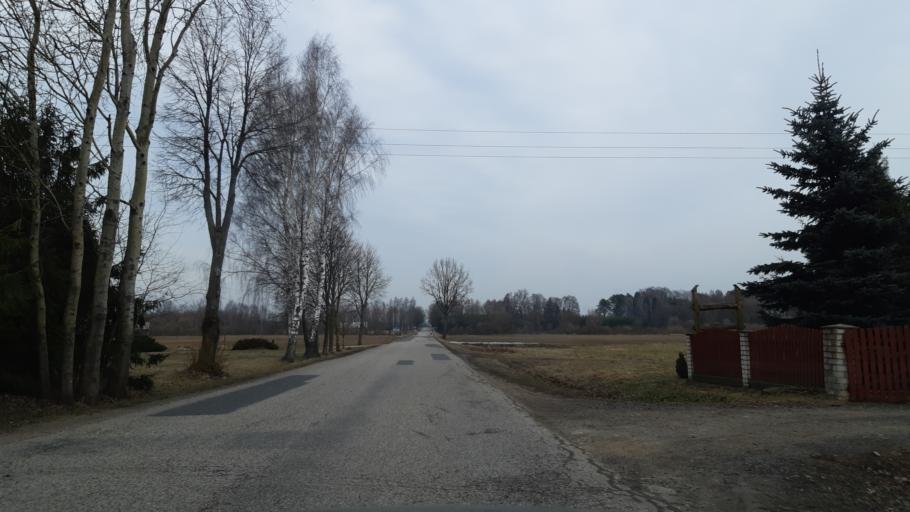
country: LT
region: Marijampoles apskritis
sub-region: Marijampole Municipality
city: Marijampole
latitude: 54.7105
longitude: 23.3156
